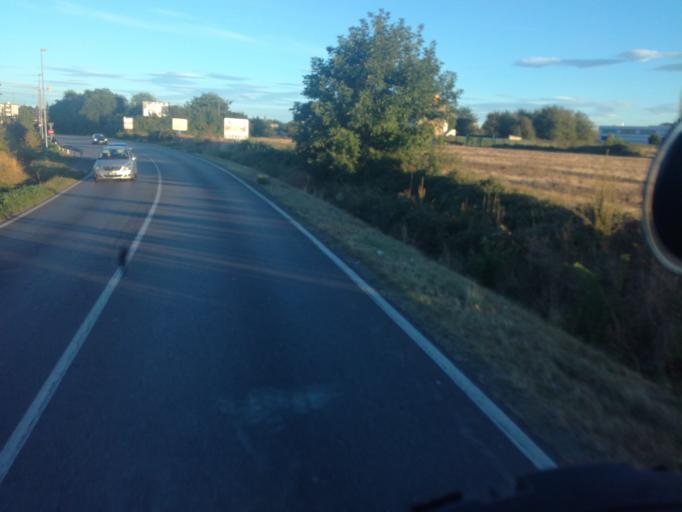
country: IT
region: Lombardy
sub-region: Provincia di Monza e Brianza
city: Varedo
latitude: 45.6037
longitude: 9.1606
